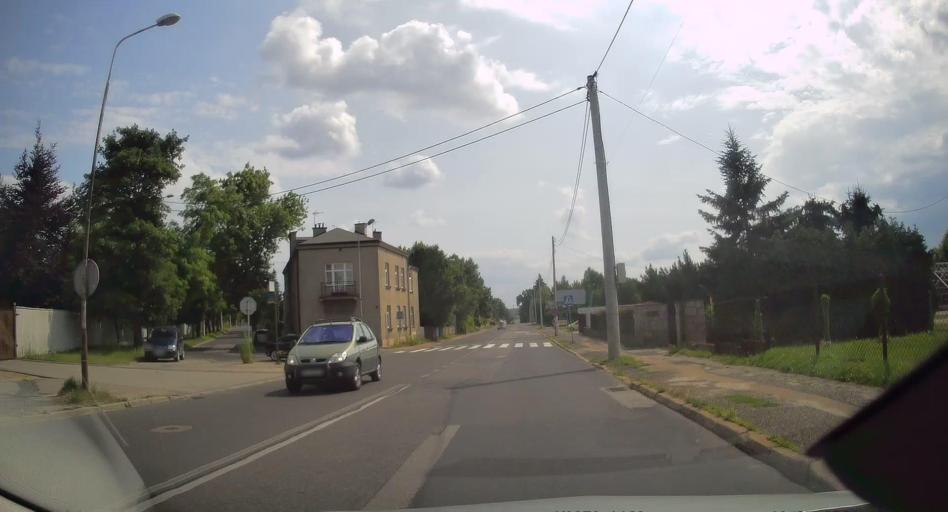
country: PL
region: Silesian Voivodeship
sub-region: Czestochowa
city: Czestochowa
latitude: 50.8127
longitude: 19.0839
